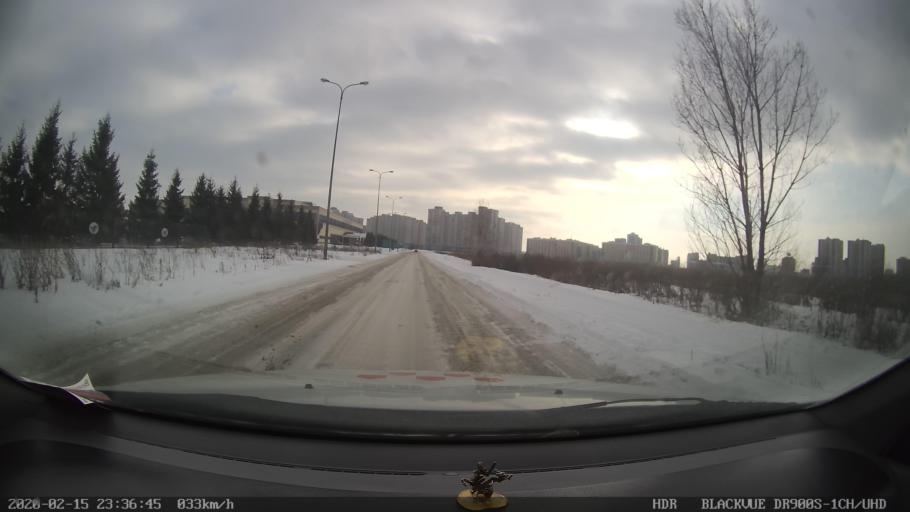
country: RU
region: Tatarstan
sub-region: Gorod Kazan'
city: Kazan
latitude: 55.7916
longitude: 49.1930
